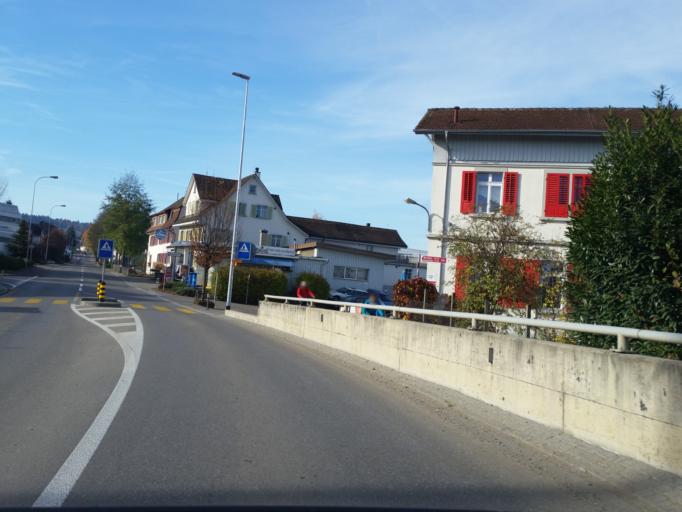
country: CH
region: Thurgau
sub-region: Kreuzlingen District
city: Tagerwilen
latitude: 47.6595
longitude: 9.1338
